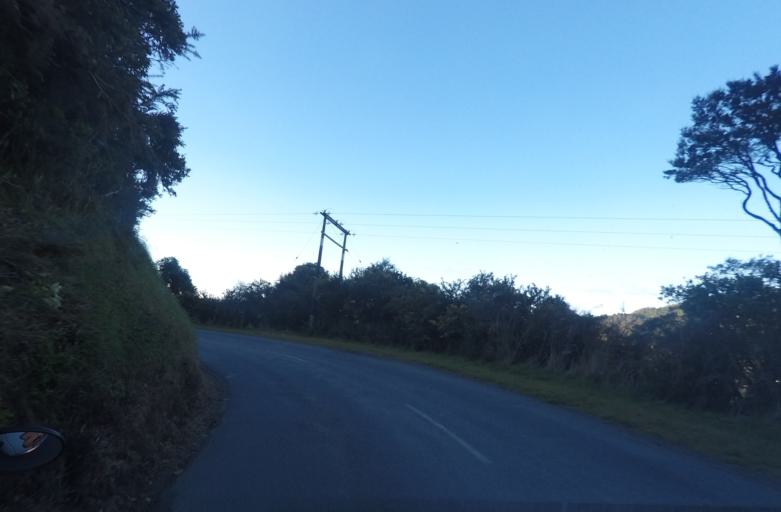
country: NZ
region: Marlborough
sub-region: Marlborough District
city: Picton
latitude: -41.2713
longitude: 173.9585
